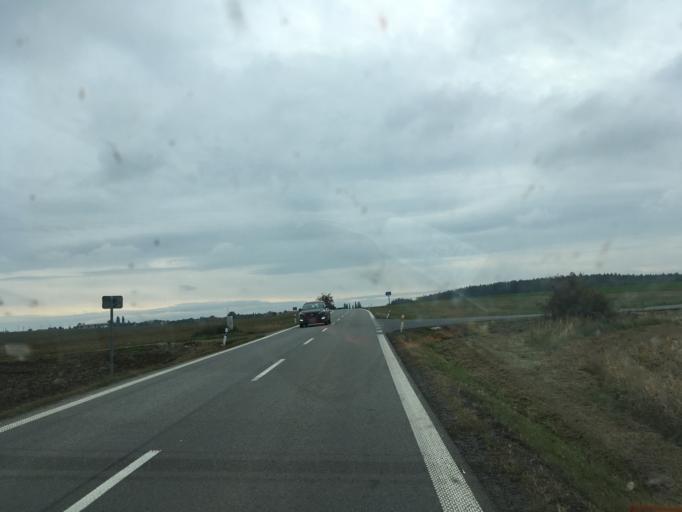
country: CZ
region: South Moravian
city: Zbraslav
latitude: 49.1944
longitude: 16.2361
